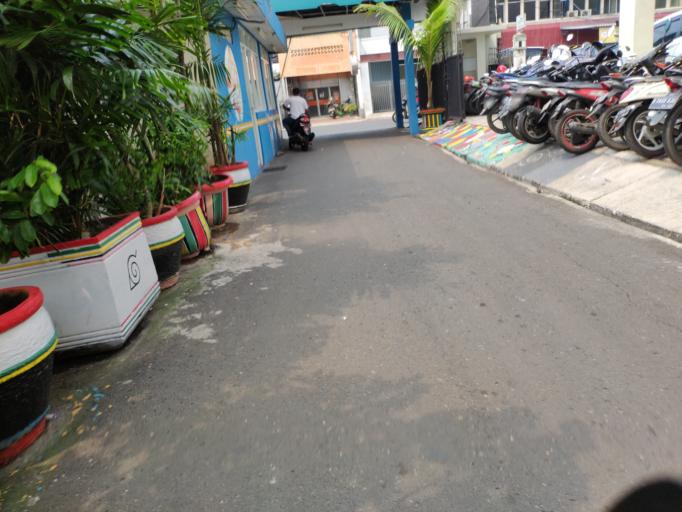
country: ID
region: Jakarta Raya
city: Jakarta
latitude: -6.1939
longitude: 106.8659
